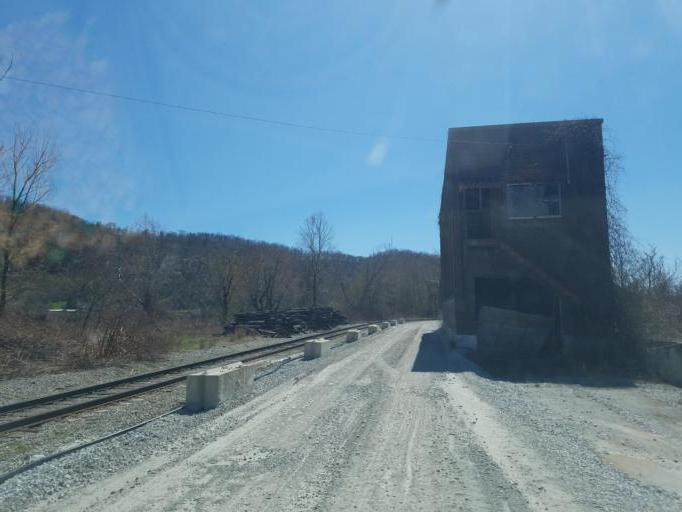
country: US
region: Ohio
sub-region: Belmont County
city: Martins Ferry
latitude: 40.1053
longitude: -80.7089
